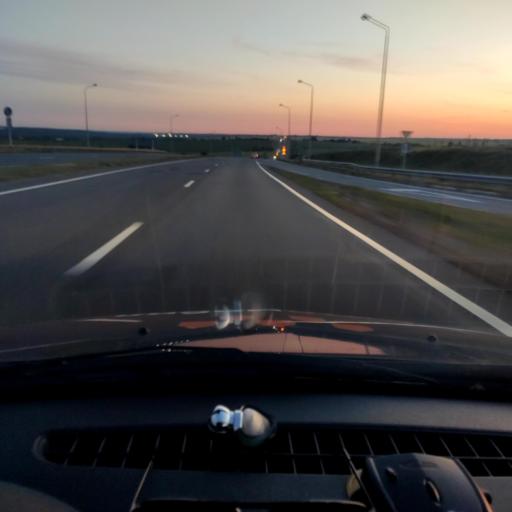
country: RU
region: Belgorod
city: Staryy Oskol
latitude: 51.3260
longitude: 37.7376
